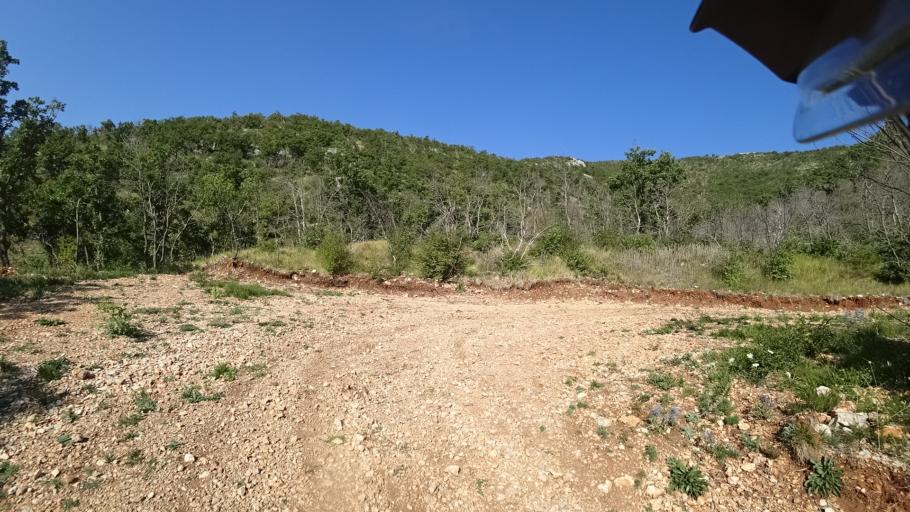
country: HR
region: Sibensko-Kniniska
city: Knin
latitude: 44.1895
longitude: 16.1631
